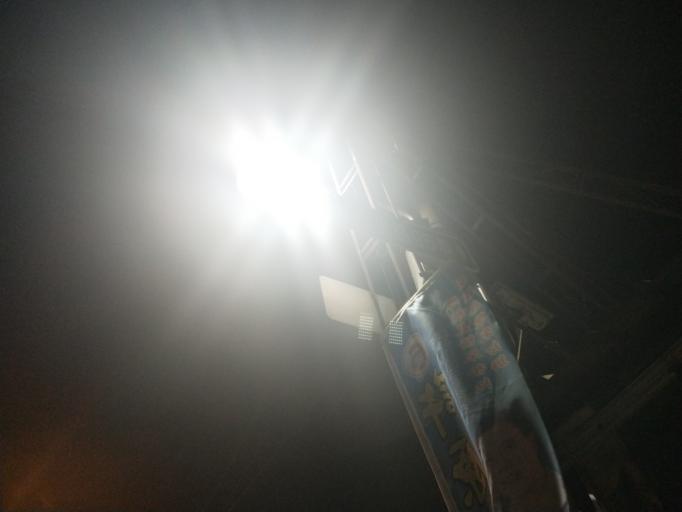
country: TW
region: Taiwan
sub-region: Changhua
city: Chang-hua
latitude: 24.0898
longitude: 120.5407
